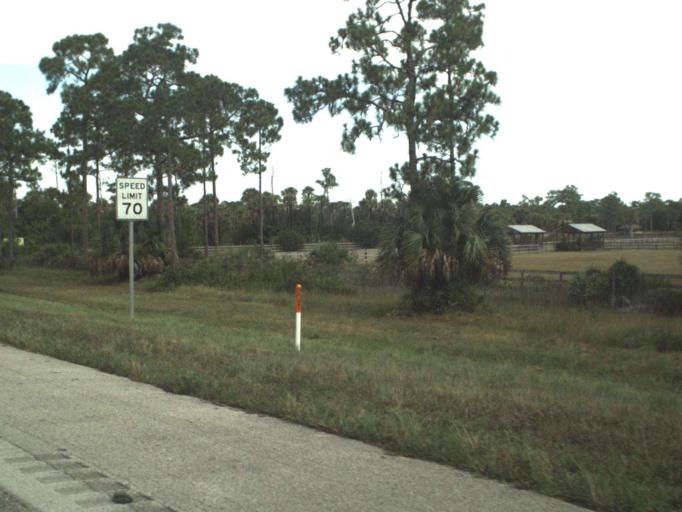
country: US
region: Florida
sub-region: Martin County
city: Palm City
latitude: 27.1282
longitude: -80.3432
